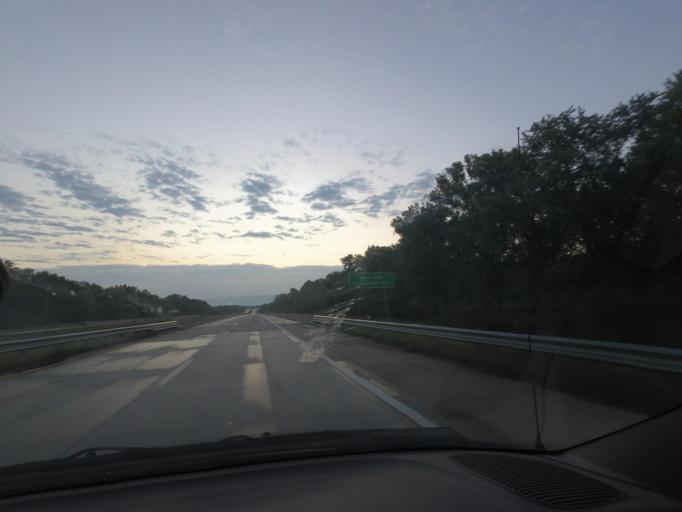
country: US
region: Missouri
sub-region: Macon County
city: Macon
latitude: 39.7586
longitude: -92.5987
